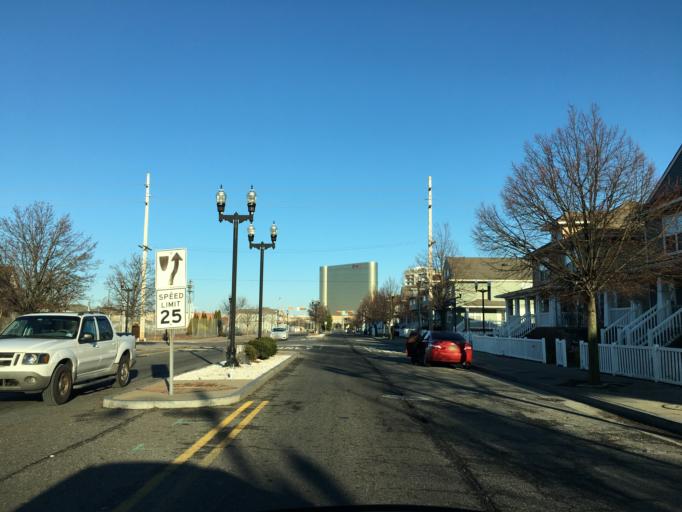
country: US
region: New Jersey
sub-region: Atlantic County
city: Atlantic City
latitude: 39.3644
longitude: -74.4263
